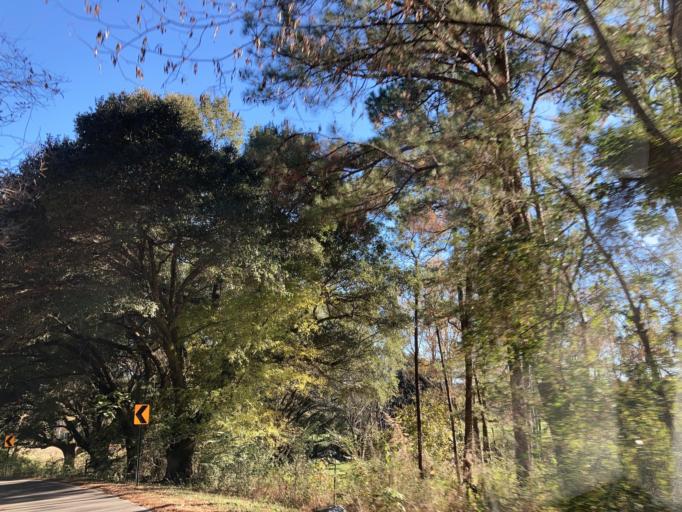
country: US
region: Mississippi
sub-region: Lamar County
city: Sumrall
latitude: 31.3681
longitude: -89.5784
